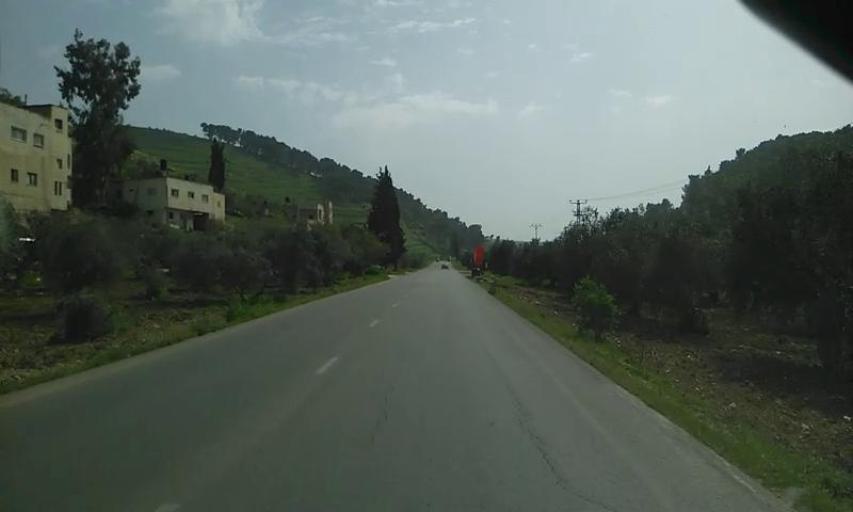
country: PS
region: West Bank
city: Mirkah
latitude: 32.4045
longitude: 35.2261
